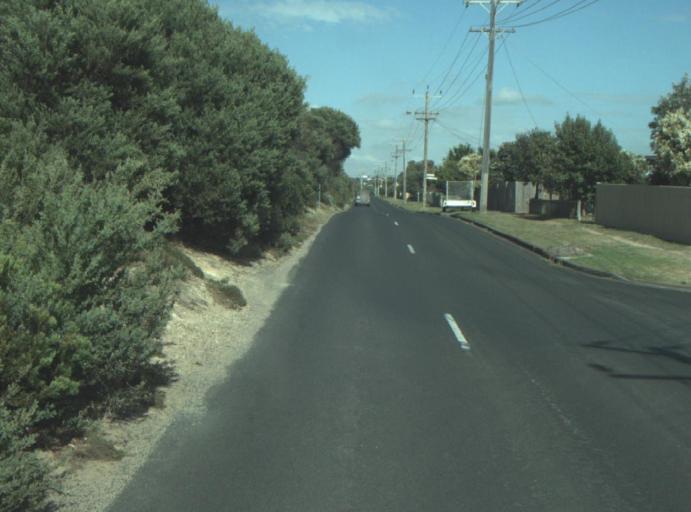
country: AU
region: Victoria
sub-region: Greater Geelong
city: Leopold
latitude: -38.2708
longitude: 144.5452
